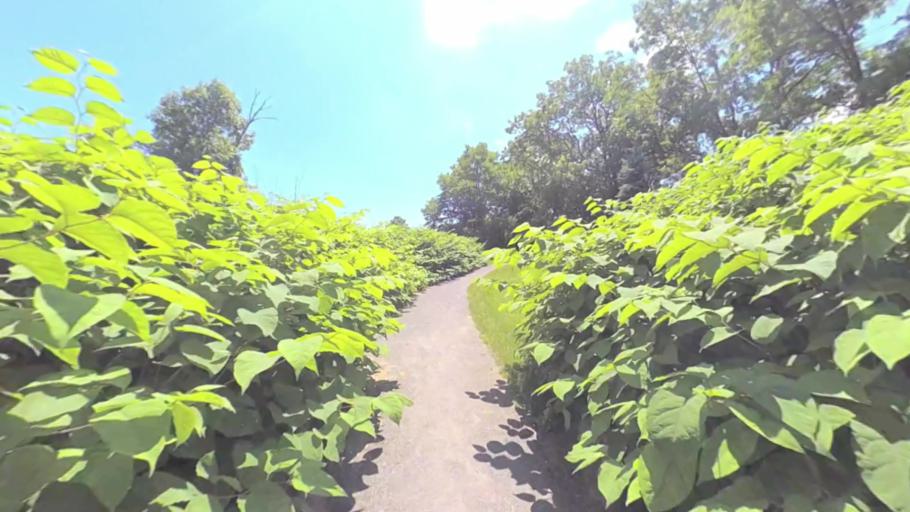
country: US
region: New York
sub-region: Monroe County
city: Fairport
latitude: 43.0986
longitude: -77.4341
